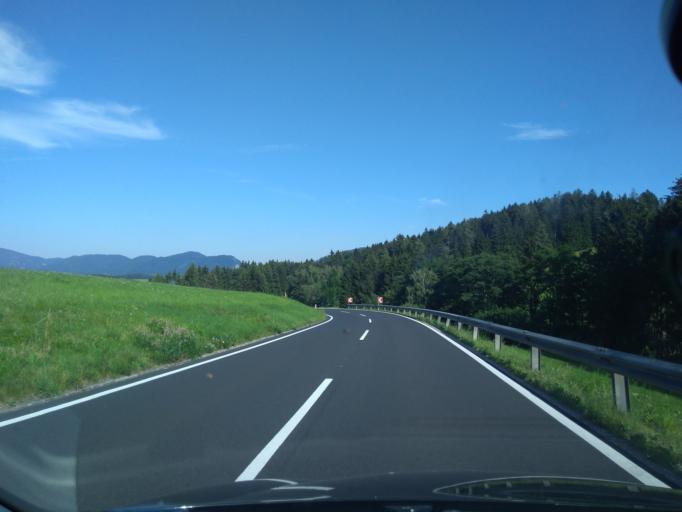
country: AT
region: Styria
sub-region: Politischer Bezirk Graz-Umgebung
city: Semriach
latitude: 47.2677
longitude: 15.4327
